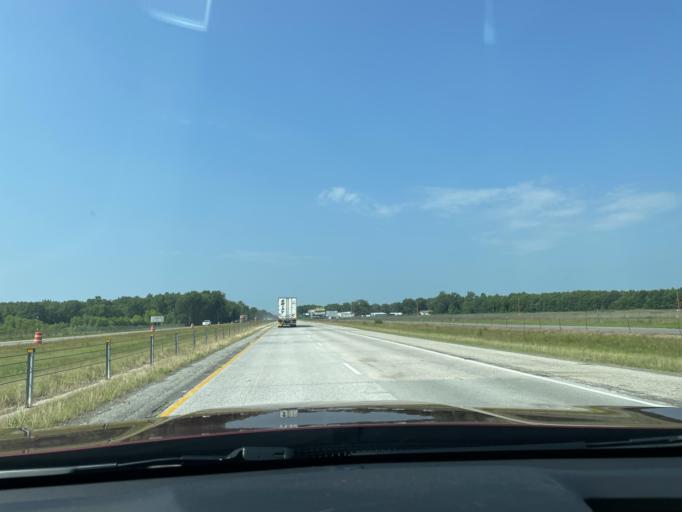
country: US
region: Arkansas
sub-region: White County
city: Searcy
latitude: 35.1986
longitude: -91.7386
